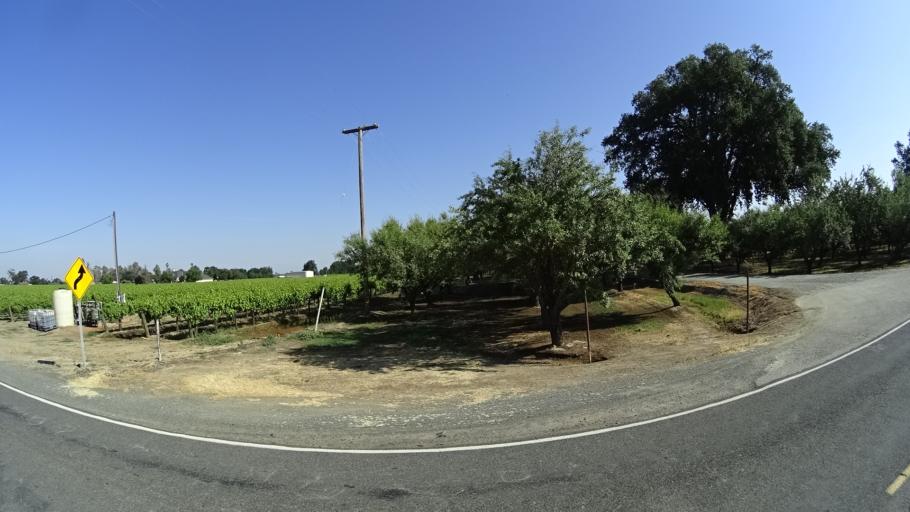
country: US
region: California
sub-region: Kings County
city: Lemoore
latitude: 36.3654
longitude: -119.8205
